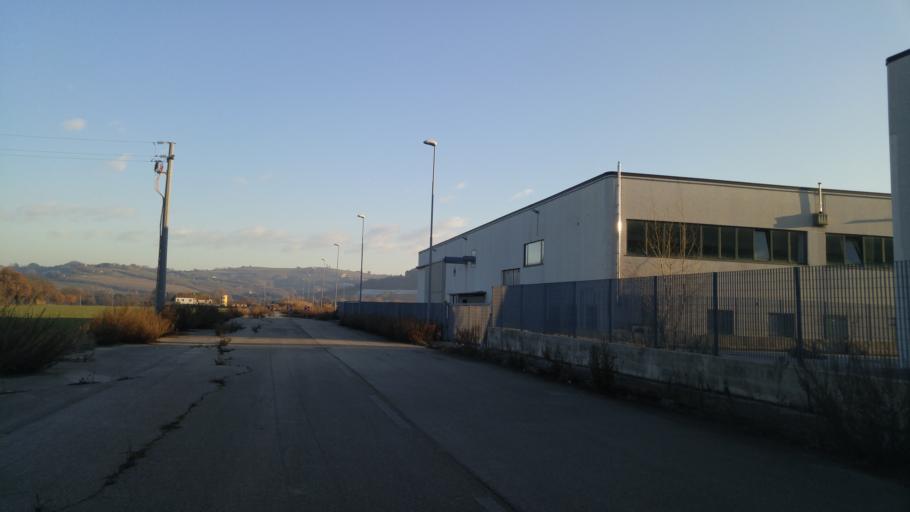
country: IT
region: The Marches
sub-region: Provincia di Ancona
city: Monterado
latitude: 43.7129
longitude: 13.0792
